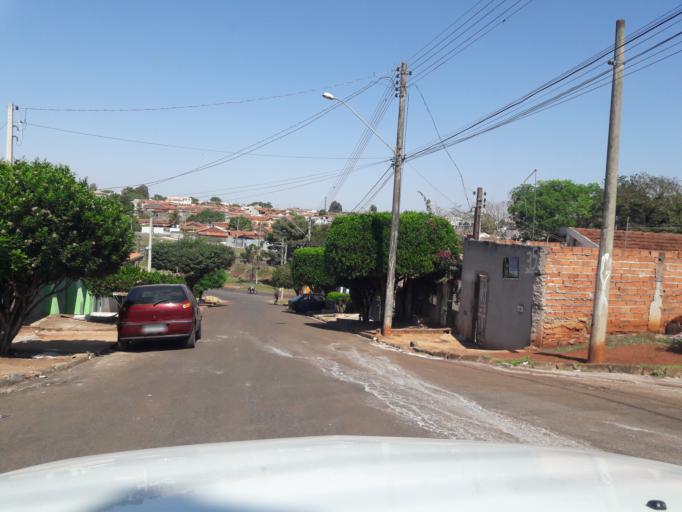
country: BR
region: Sao Paulo
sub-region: Moji-Guacu
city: Mogi-Gaucu
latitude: -22.3404
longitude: -46.9345
